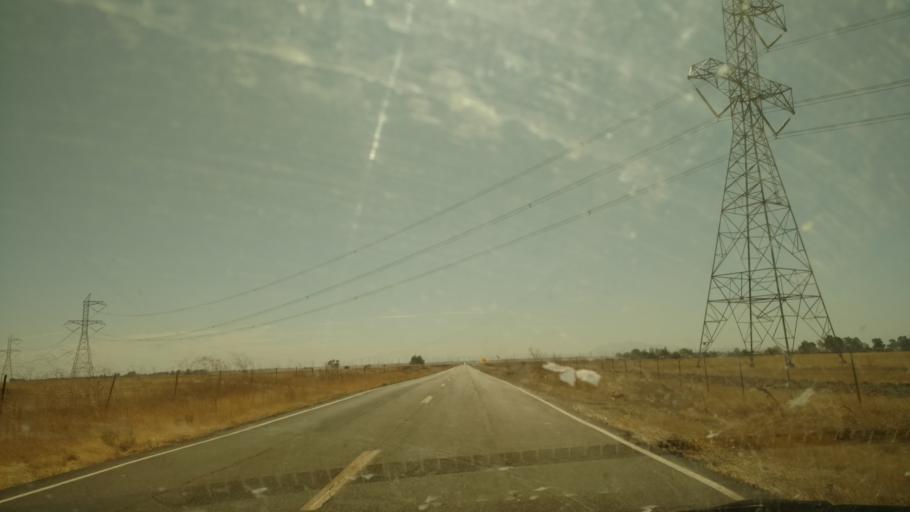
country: US
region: California
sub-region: Solano County
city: Rio Vista
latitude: 38.2539
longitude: -121.8055
